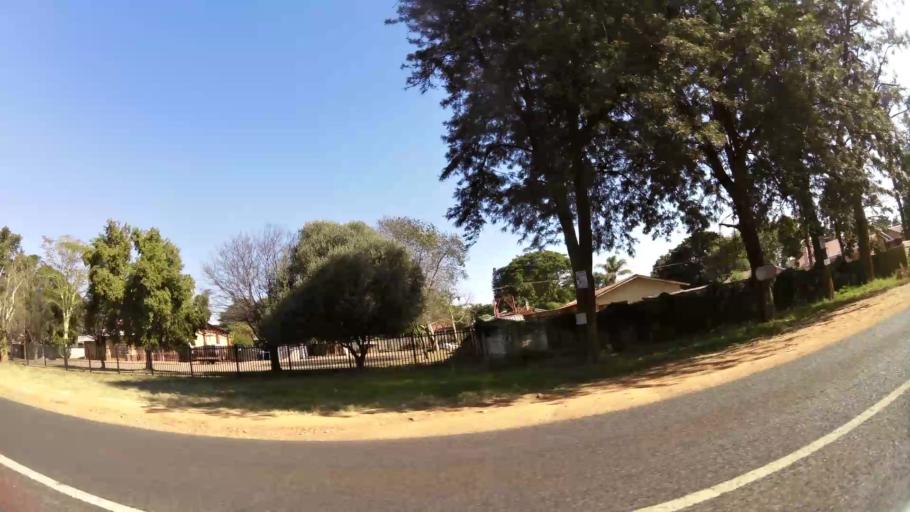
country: ZA
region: North-West
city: Ga-Rankuwa
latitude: -25.6478
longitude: 28.1026
